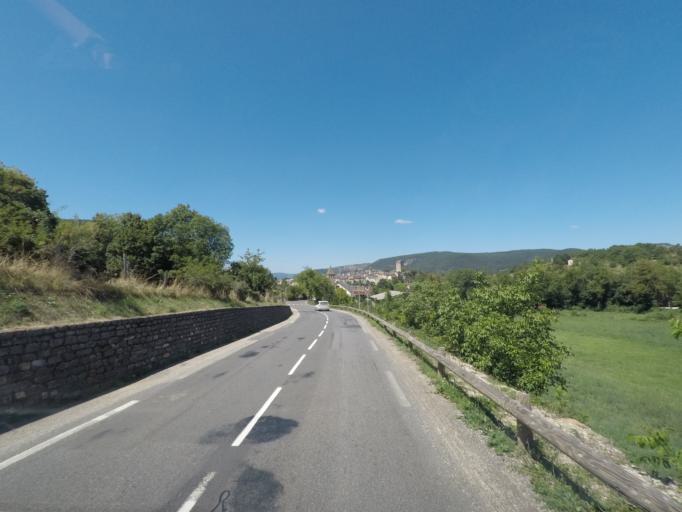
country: FR
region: Languedoc-Roussillon
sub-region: Departement de la Lozere
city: Chanac
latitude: 44.4624
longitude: 3.3483
